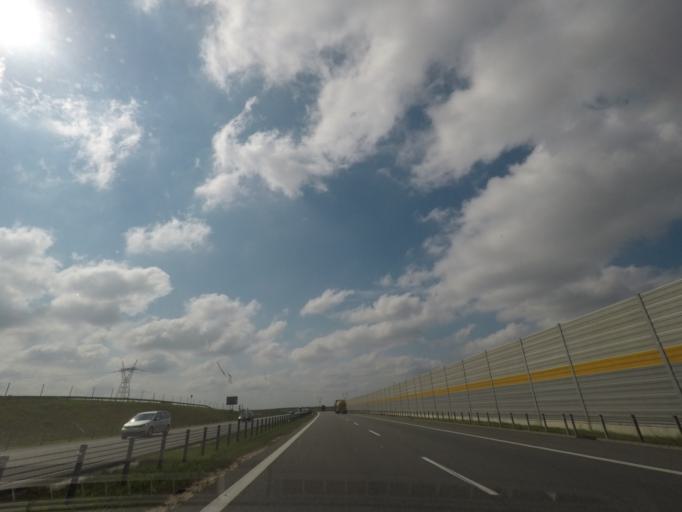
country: PL
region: Kujawsko-Pomorskie
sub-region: Powiat chelminski
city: Lisewo
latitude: 53.2377
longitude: 18.7254
